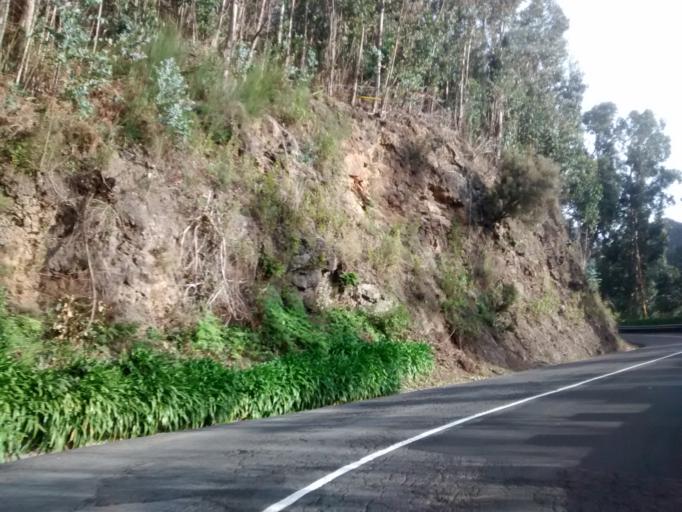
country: PT
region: Madeira
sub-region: Sao Vicente
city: Sao Vicente
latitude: 32.7458
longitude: -17.0259
